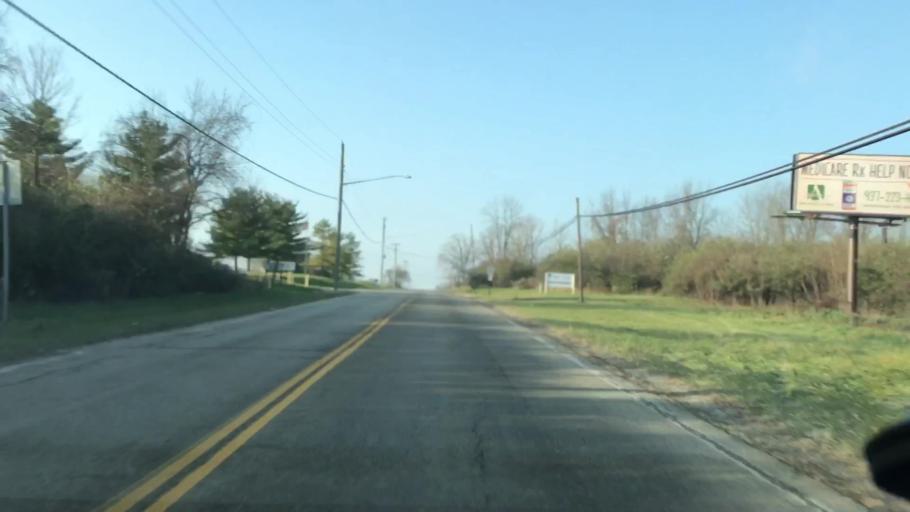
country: US
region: Ohio
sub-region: Greene County
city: Fairborn
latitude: 39.8419
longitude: -84.0007
